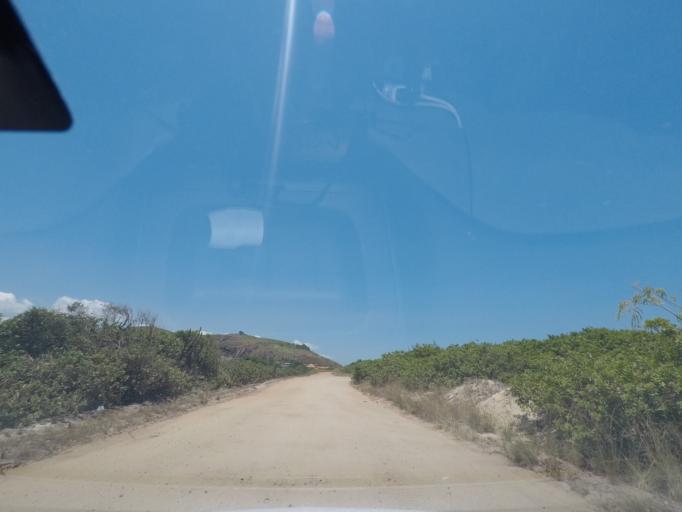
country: BR
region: Rio de Janeiro
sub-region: Niteroi
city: Niteroi
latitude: -22.9688
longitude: -43.0064
